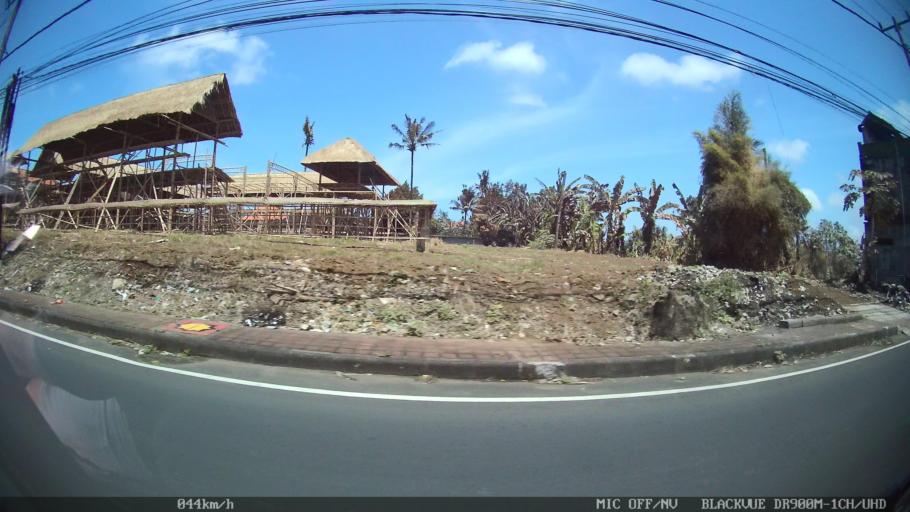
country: ID
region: Bali
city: Banjar Sedang
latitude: -8.5660
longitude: 115.3060
